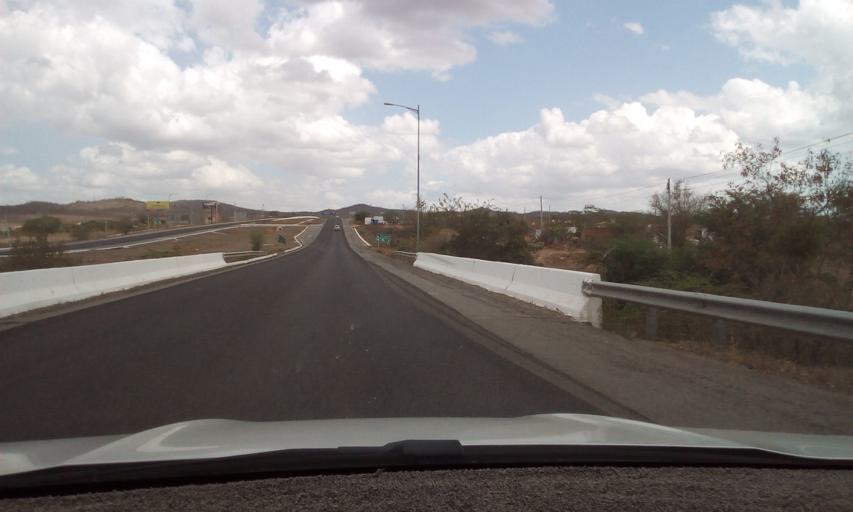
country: BR
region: Pernambuco
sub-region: Toritama
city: Toritama
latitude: -8.1085
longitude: -36.0203
